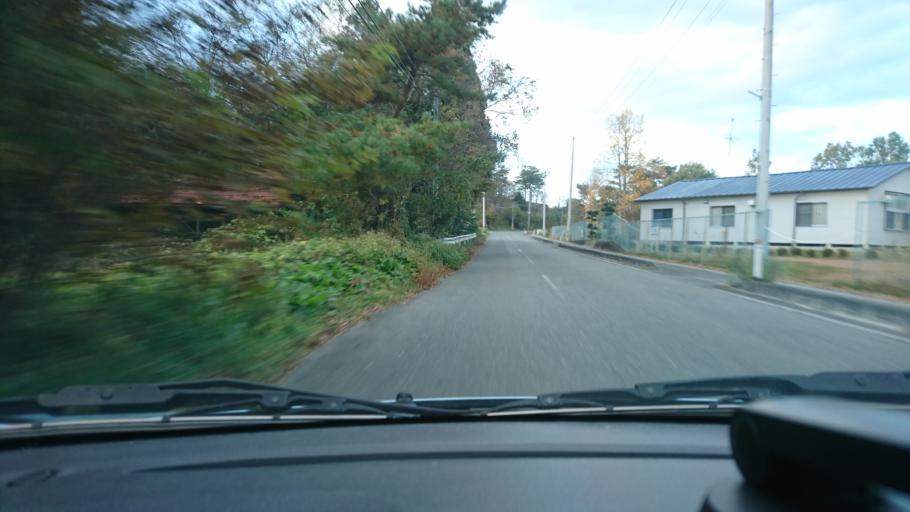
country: JP
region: Iwate
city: Ichinoseki
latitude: 38.7968
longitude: 141.1927
